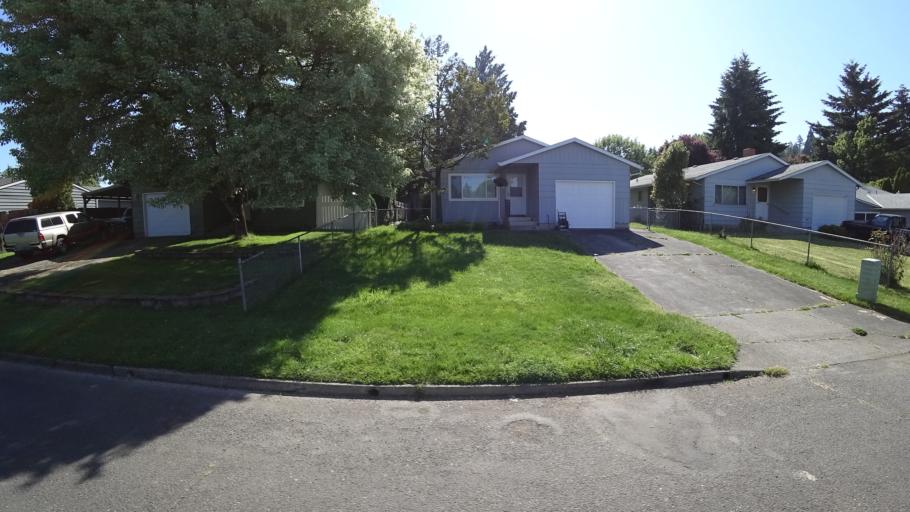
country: US
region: Oregon
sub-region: Multnomah County
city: Lents
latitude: 45.4663
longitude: -122.5578
